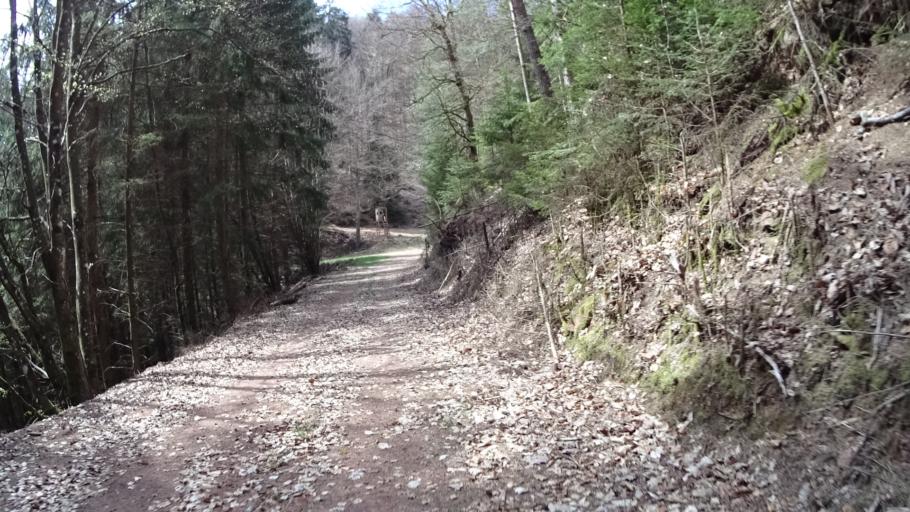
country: DE
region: Rheinland-Pfalz
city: Ramberg
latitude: 49.3137
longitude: 7.9944
